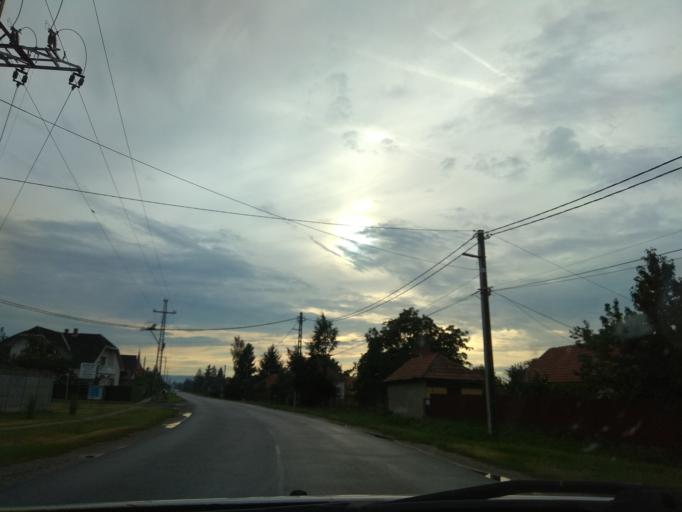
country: HU
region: Borsod-Abauj-Zemplen
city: Onga
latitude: 48.1214
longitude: 20.9164
